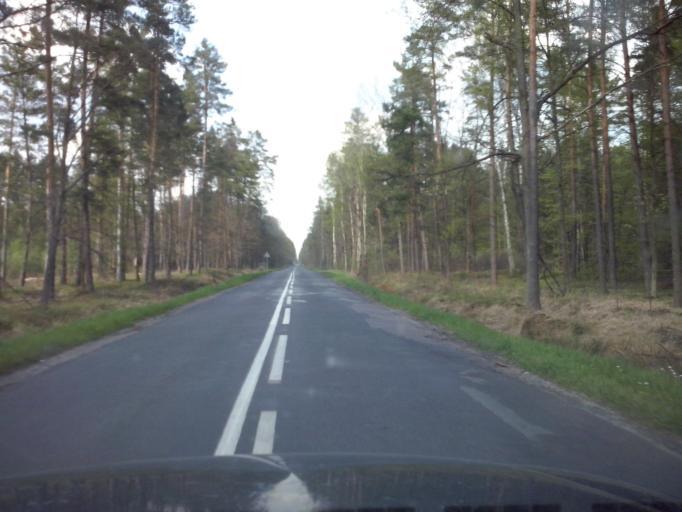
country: PL
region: Subcarpathian Voivodeship
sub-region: Powiat lezajski
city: Letownia
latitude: 50.3659
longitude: 22.2461
